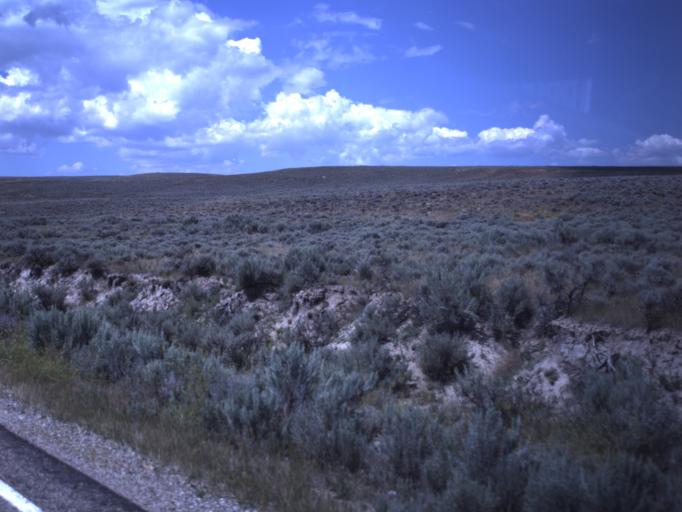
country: US
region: Utah
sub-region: Rich County
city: Randolph
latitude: 41.7707
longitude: -111.1416
